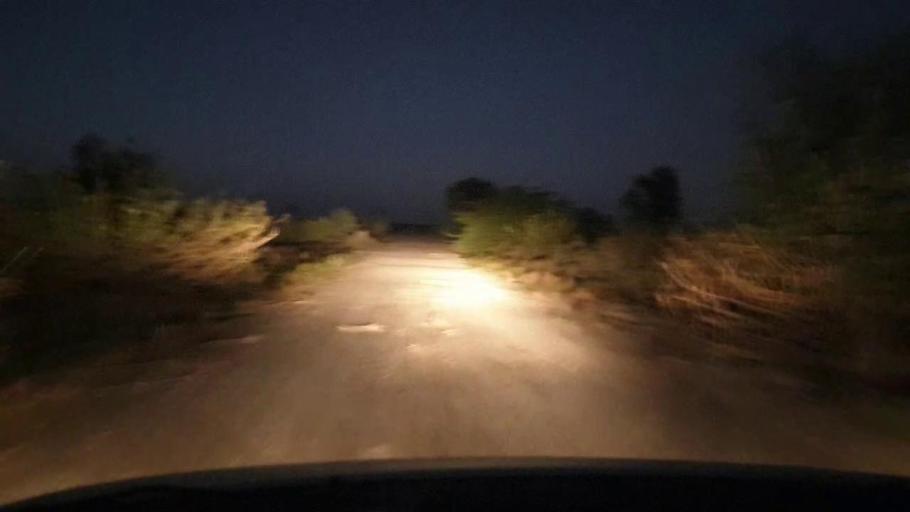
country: PK
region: Sindh
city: Phulji
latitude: 26.9156
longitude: 67.4810
